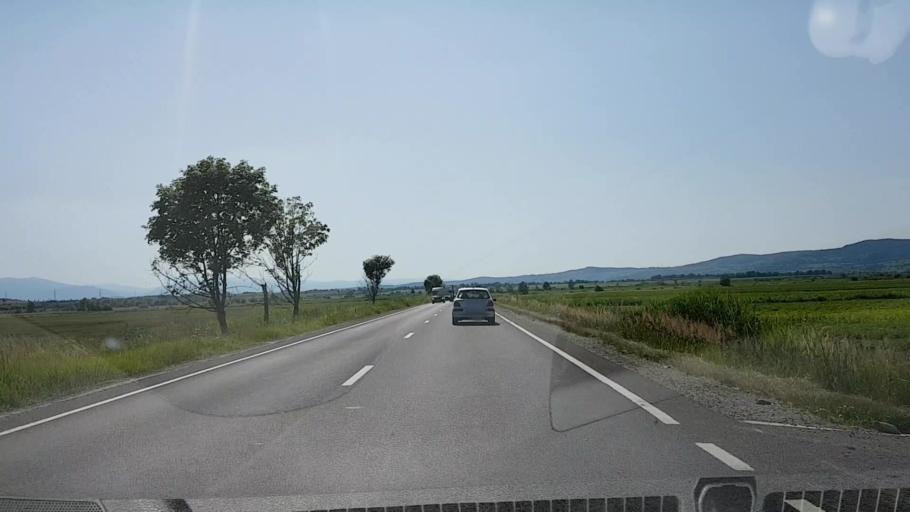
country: RO
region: Sibiu
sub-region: Comuna Porumbacu de Jos
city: Porumbacu de Jos
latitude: 45.7561
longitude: 24.4991
